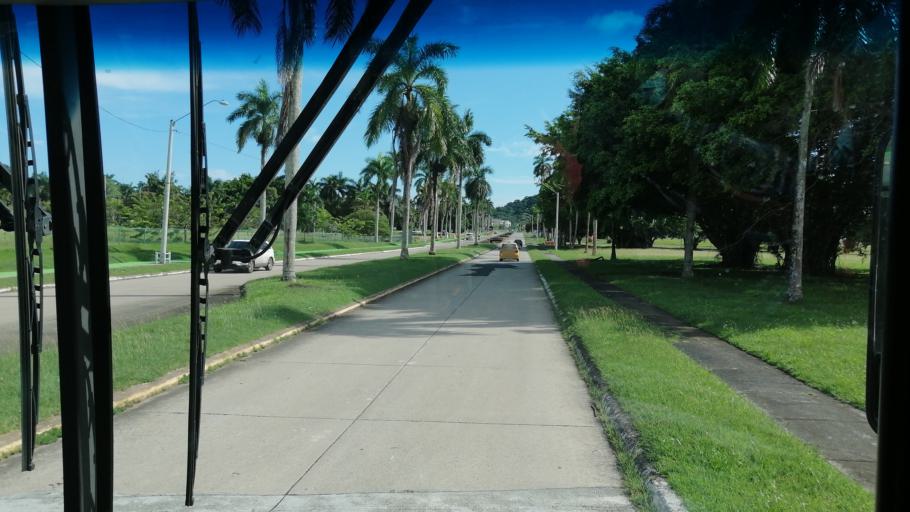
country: PA
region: Panama
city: Veracruz
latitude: 8.9157
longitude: -79.5920
